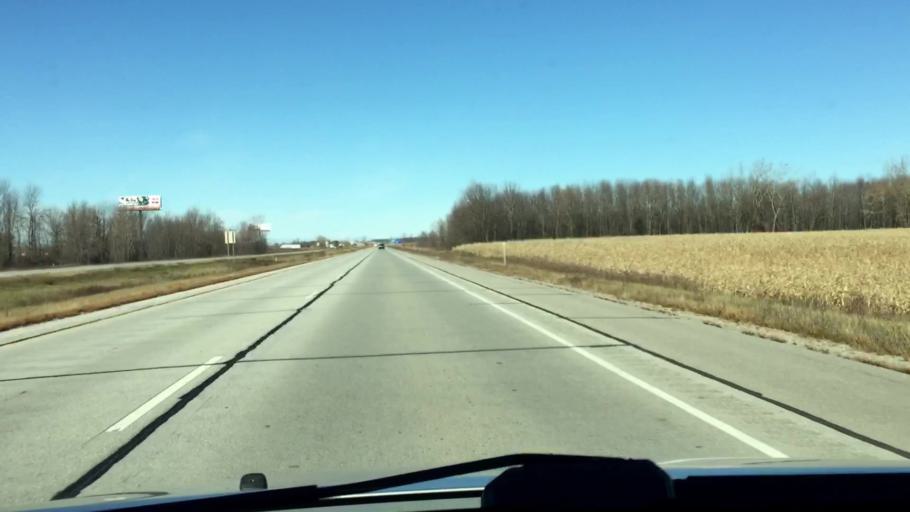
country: US
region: Wisconsin
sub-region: Brown County
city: Pulaski
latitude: 44.5899
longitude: -88.2018
